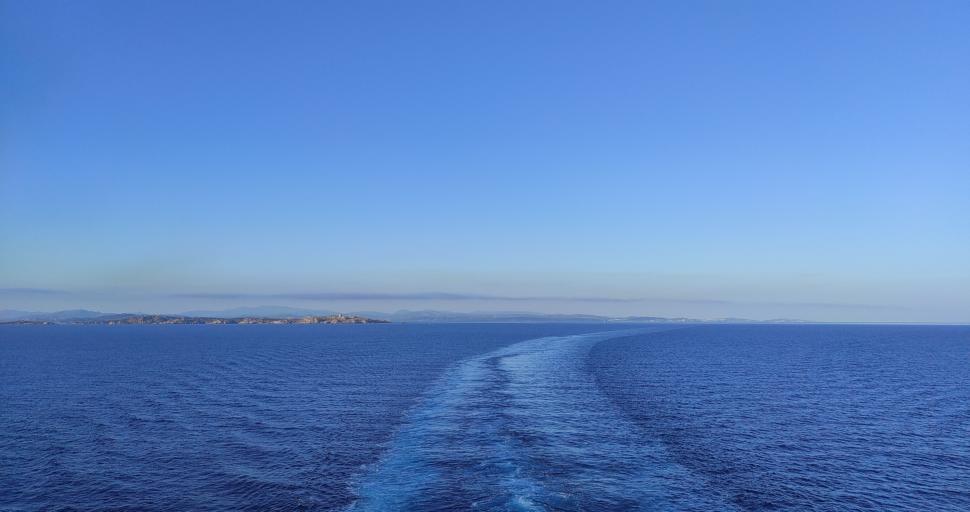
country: IT
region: Sardinia
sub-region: Provincia di Olbia-Tempio
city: La Maddalena
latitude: 41.3523
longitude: 9.3629
